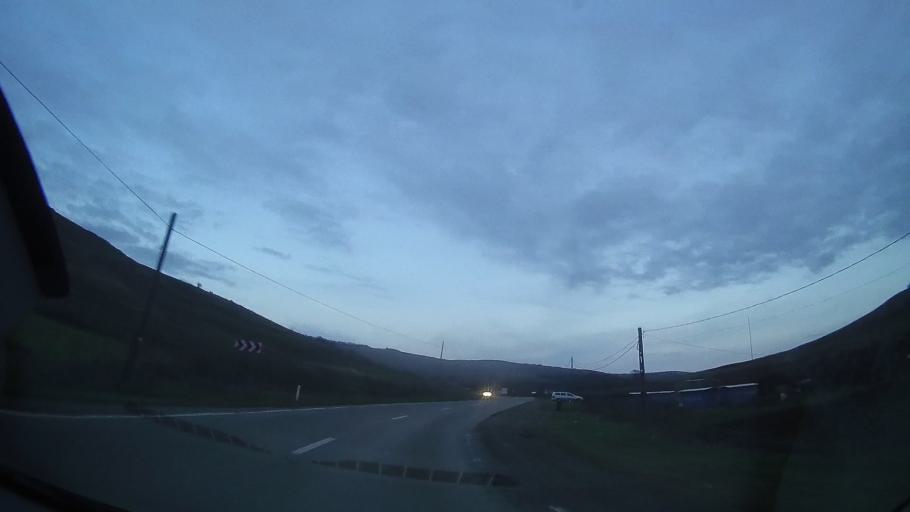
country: RO
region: Cluj
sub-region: Comuna Caianu
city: Vaida-Camaras
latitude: 46.8037
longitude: 23.9590
